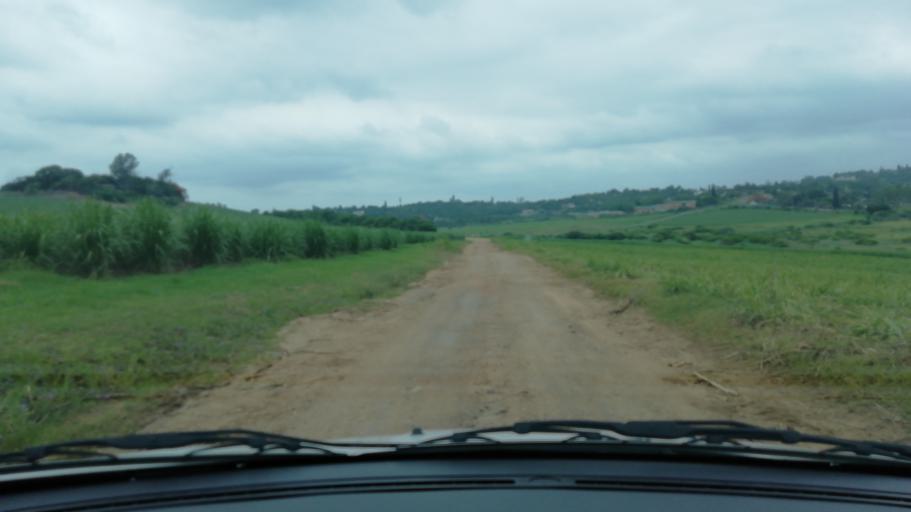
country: ZA
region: KwaZulu-Natal
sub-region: uThungulu District Municipality
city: Empangeni
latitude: -28.7343
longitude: 31.9079
